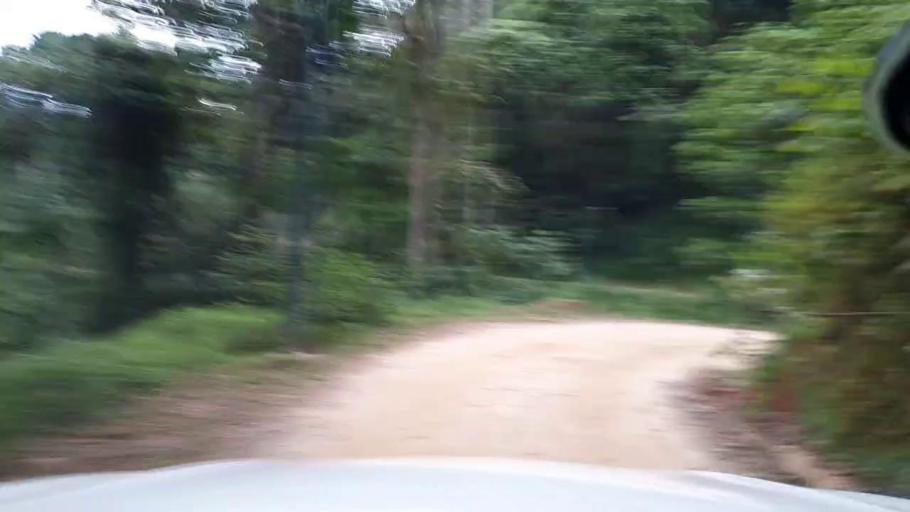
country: RW
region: Southern Province
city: Nzega
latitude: -2.5537
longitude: 29.2362
